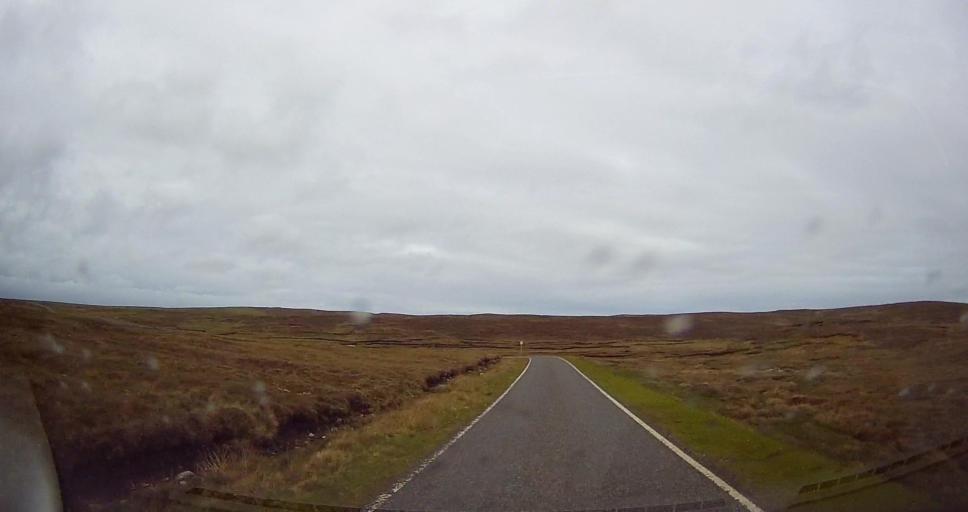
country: GB
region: Scotland
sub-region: Shetland Islands
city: Lerwick
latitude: 60.4913
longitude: -1.5769
